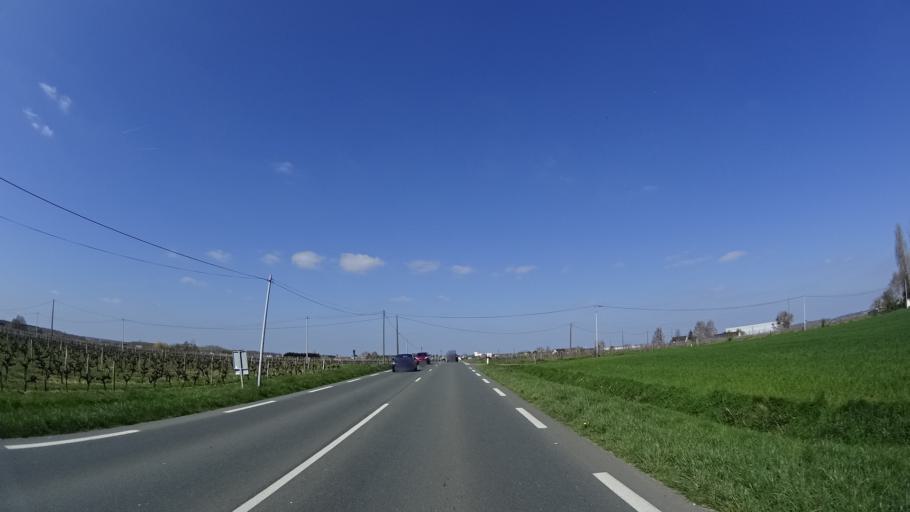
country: FR
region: Pays de la Loire
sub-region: Departement de Maine-et-Loire
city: Brissac-Quince
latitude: 47.3358
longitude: -0.4279
